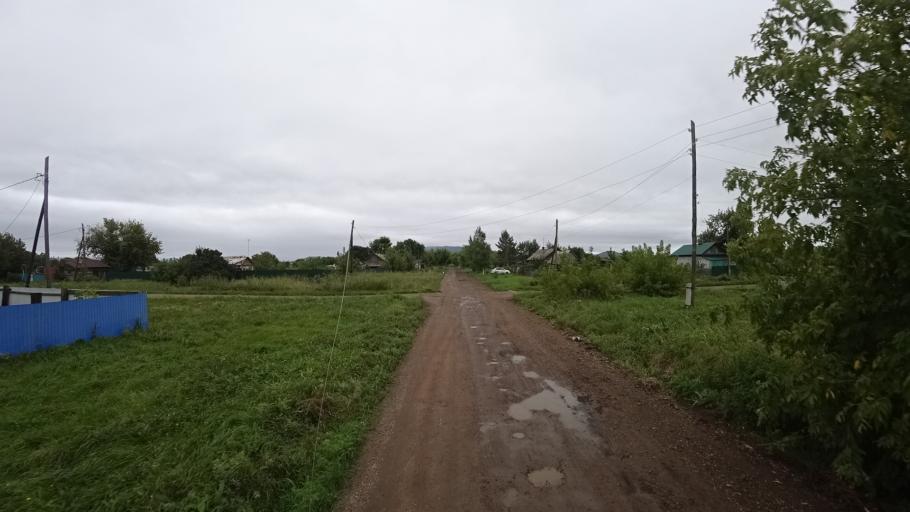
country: RU
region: Primorskiy
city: Chernigovka
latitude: 44.3409
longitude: 132.5482
